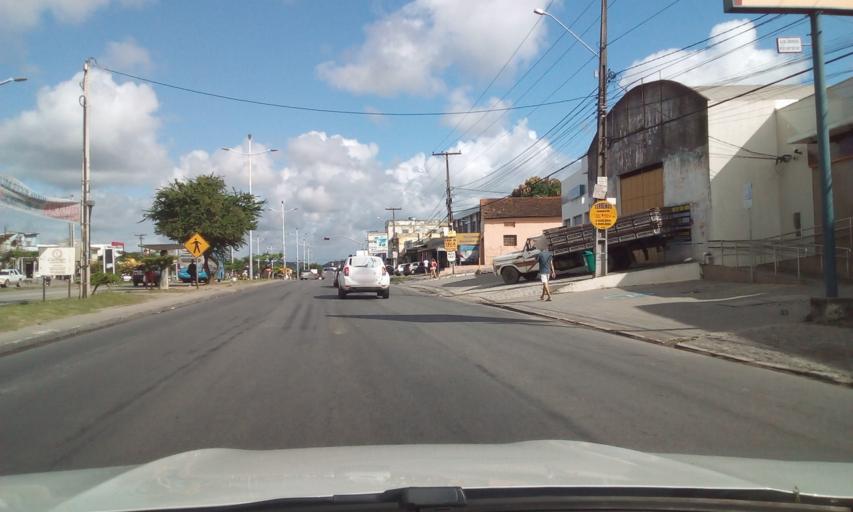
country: BR
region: Pernambuco
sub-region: Igarassu
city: Igarassu
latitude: -7.8717
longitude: -34.9065
